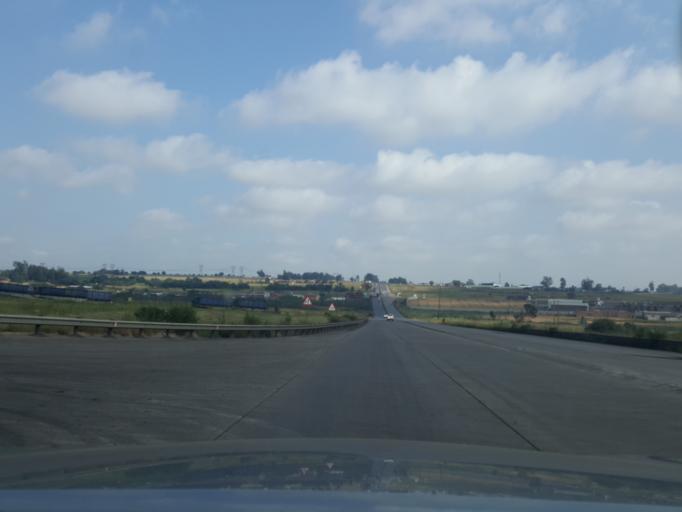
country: ZA
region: Mpumalanga
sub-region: Nkangala District Municipality
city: Witbank
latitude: -25.9621
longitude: 29.2609
